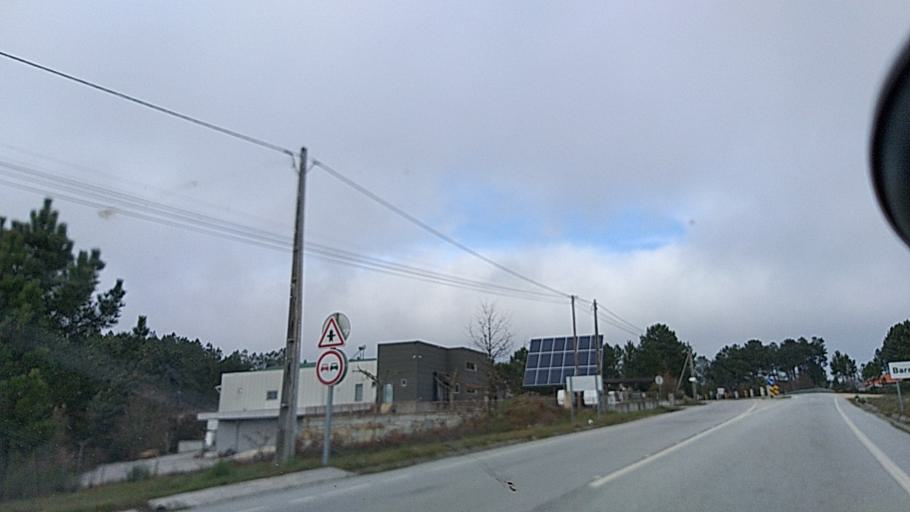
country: PT
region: Guarda
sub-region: Aguiar da Beira
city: Aguiar da Beira
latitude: 40.7878
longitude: -7.5031
